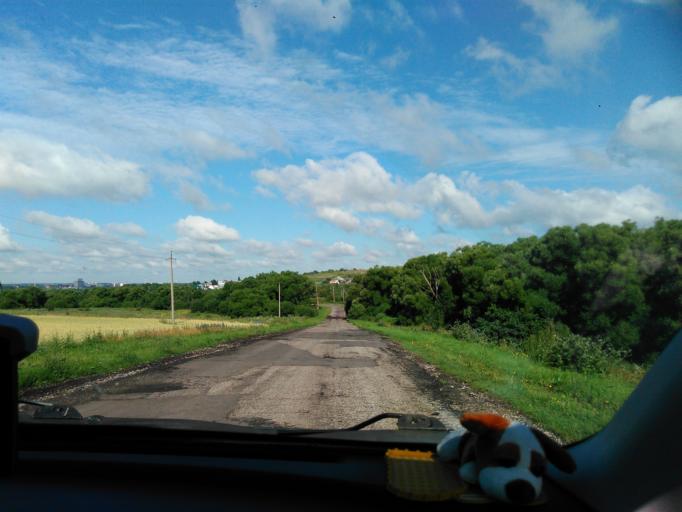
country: RU
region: Penza
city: Lermontovo
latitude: 53.1791
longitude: 44.0926
